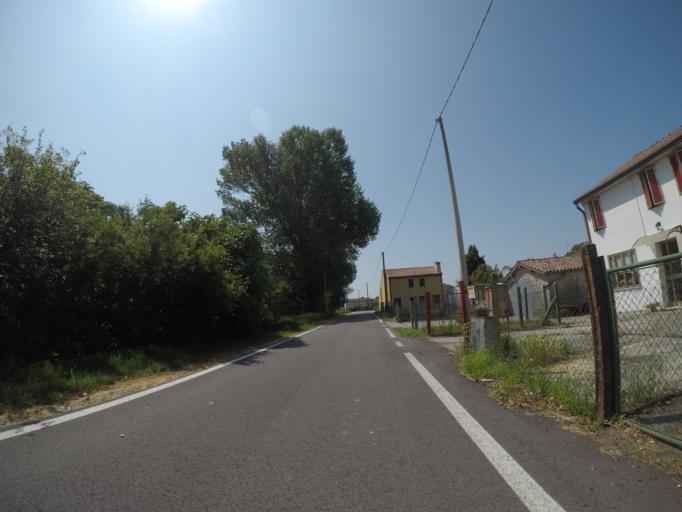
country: IT
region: Veneto
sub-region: Provincia di Rovigo
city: Fratta Polesine
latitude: 45.0173
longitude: 11.6405
